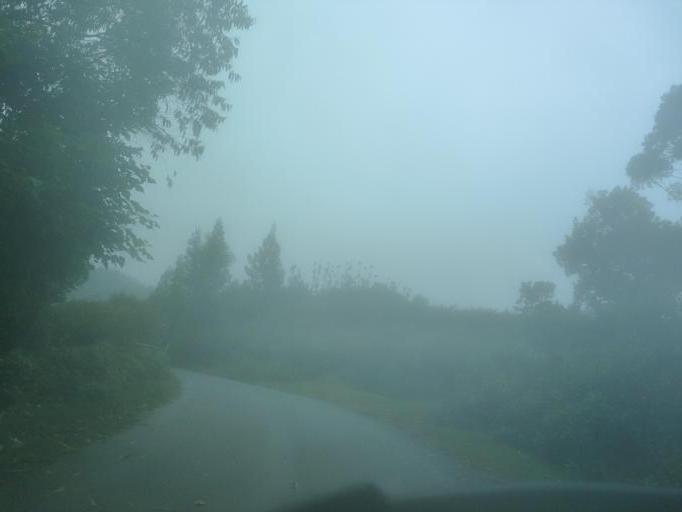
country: IN
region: Tamil Nadu
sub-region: Dindigul
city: Kodaikanal
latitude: 10.2036
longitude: 77.3469
